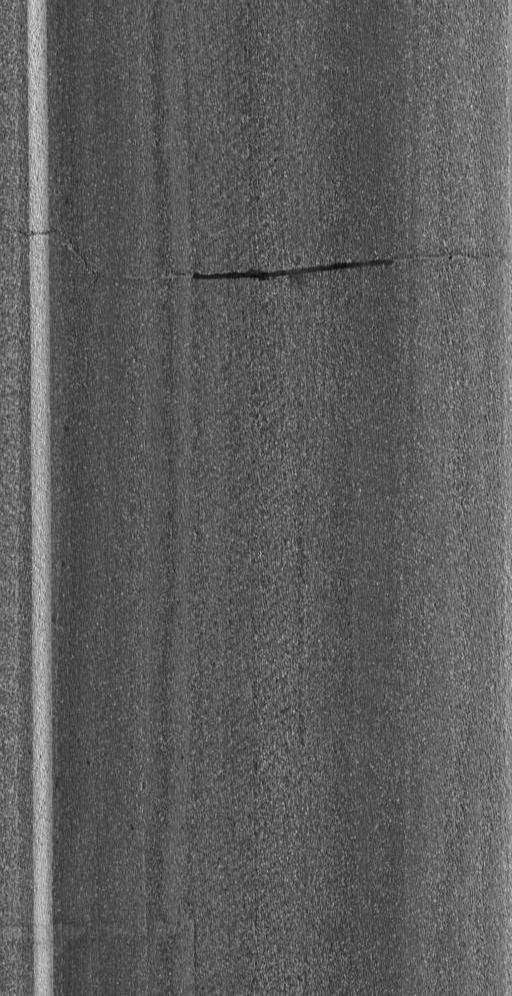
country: US
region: Vermont
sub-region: Franklin County
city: Saint Albans
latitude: 44.7945
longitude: -73.0686
